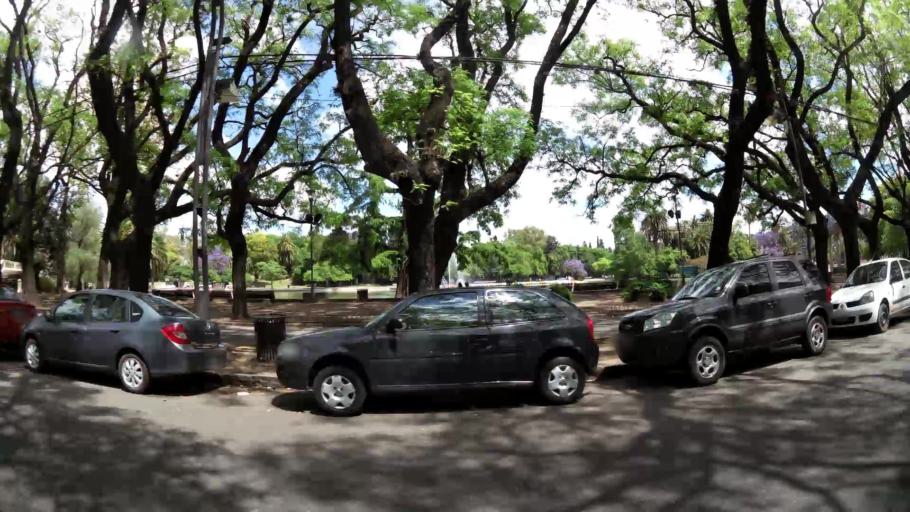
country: AR
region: Santa Fe
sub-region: Departamento de Rosario
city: Rosario
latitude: -32.9571
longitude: -60.6568
